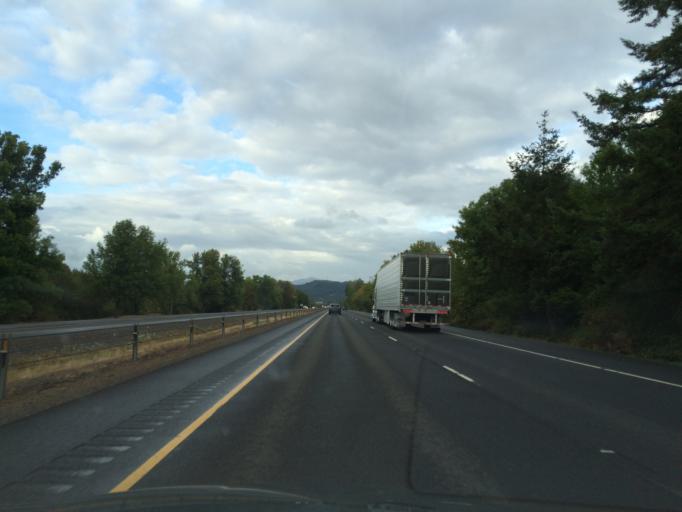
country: US
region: Oregon
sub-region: Lane County
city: Cottage Grove
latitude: 43.7528
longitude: -123.1054
